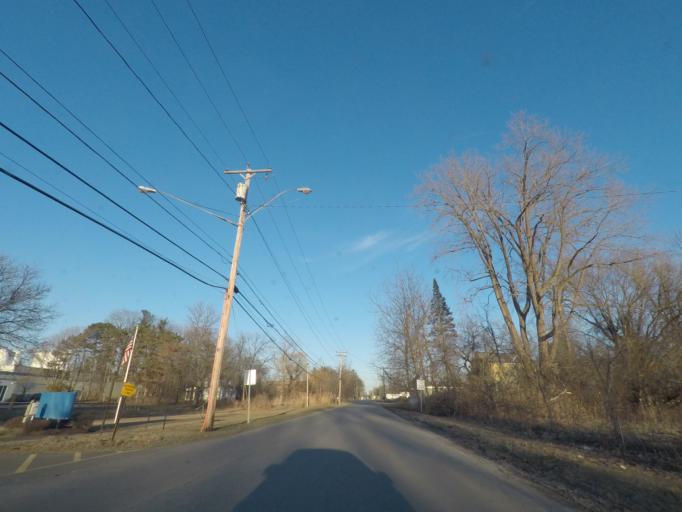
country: US
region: New York
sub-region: Albany County
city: Colonie
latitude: 42.7391
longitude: -73.7965
